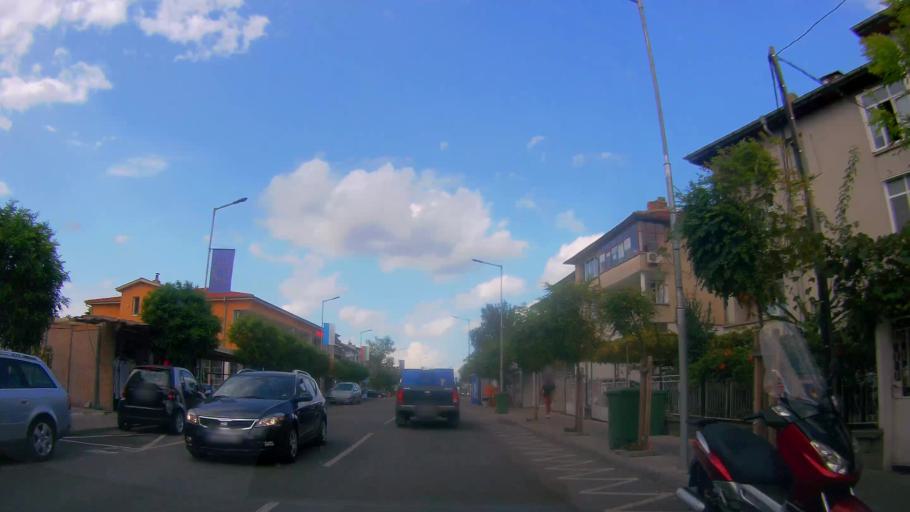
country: BG
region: Burgas
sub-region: Obshtina Primorsko
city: Primorsko
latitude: 42.2676
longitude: 27.7494
